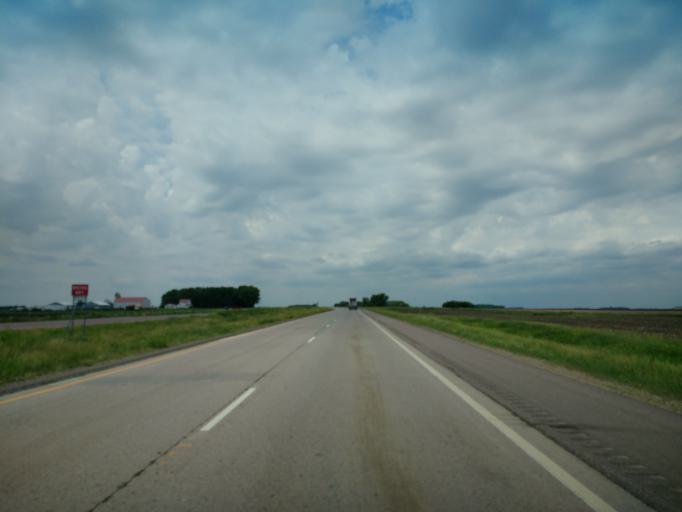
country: US
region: Minnesota
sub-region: Cottonwood County
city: Mountain Lake
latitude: 43.9495
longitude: -94.8406
